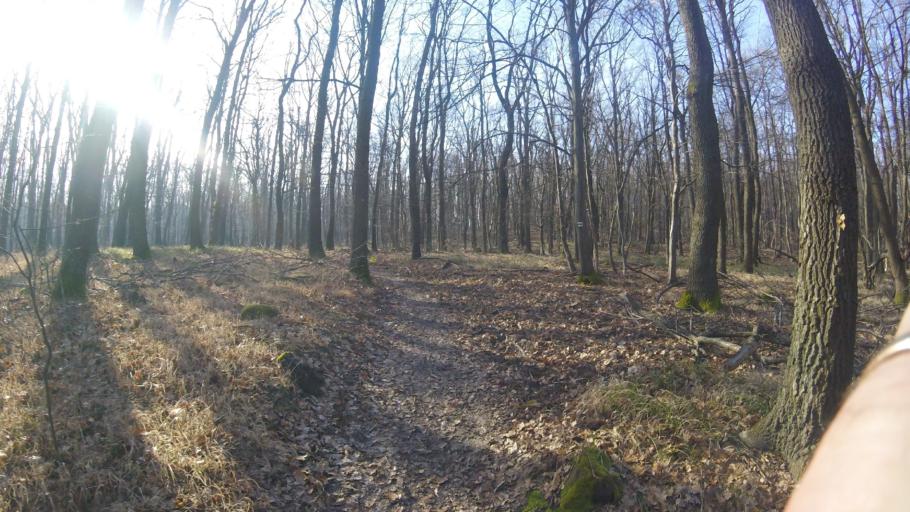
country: HU
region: Pest
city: Pilisszentkereszt
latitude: 47.6700
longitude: 18.9127
